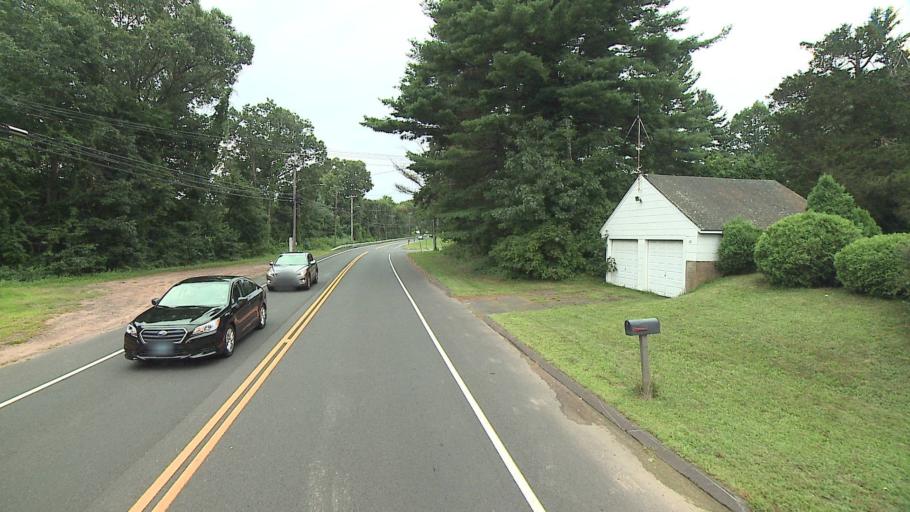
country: US
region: Connecticut
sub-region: Middlesex County
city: Cromwell
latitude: 41.6234
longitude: -72.6755
